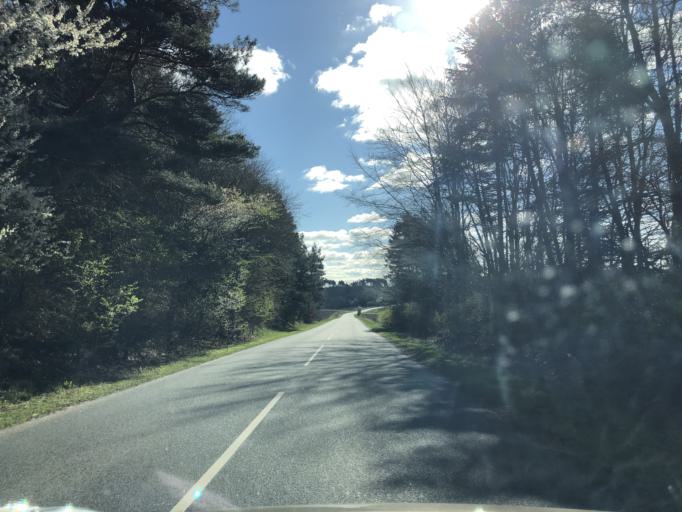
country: DK
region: North Denmark
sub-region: Vesthimmerland Kommune
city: Alestrup
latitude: 56.6127
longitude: 9.5295
